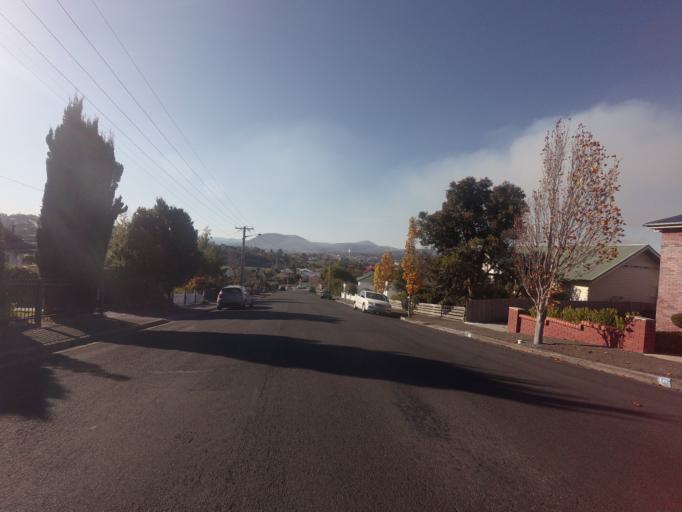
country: AU
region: Tasmania
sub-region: Hobart
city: New Town
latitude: -42.8661
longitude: 147.2939
